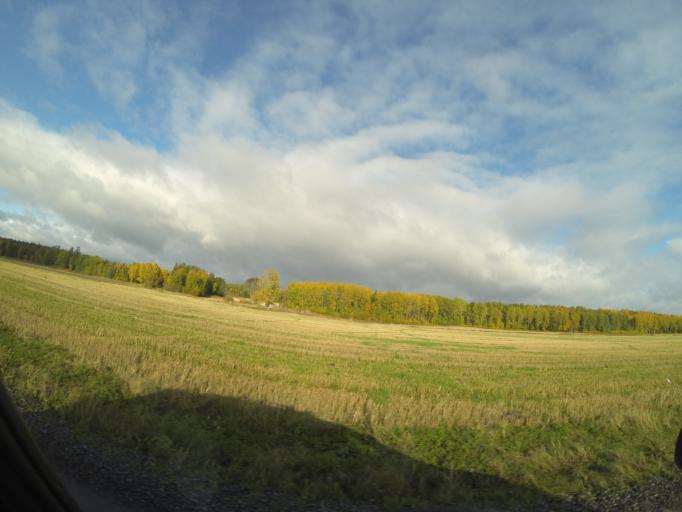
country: SE
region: Soedermanland
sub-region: Eskilstuna Kommun
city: Kvicksund
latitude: 59.3789
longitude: 16.2575
